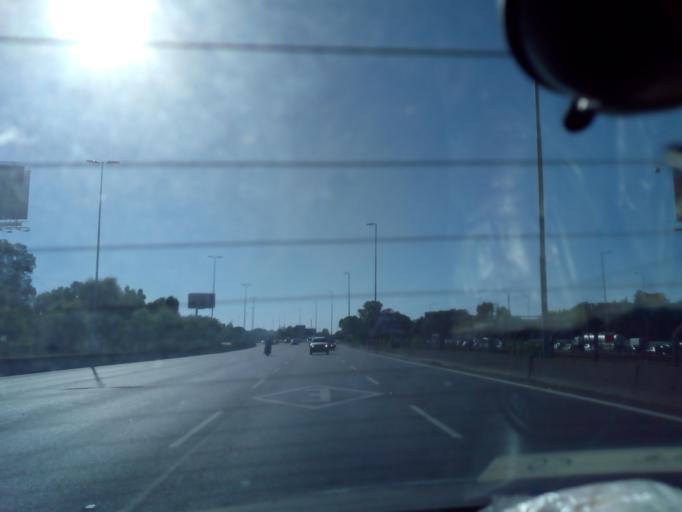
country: AR
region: Buenos Aires F.D.
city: Colegiales
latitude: -34.5387
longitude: -58.4566
